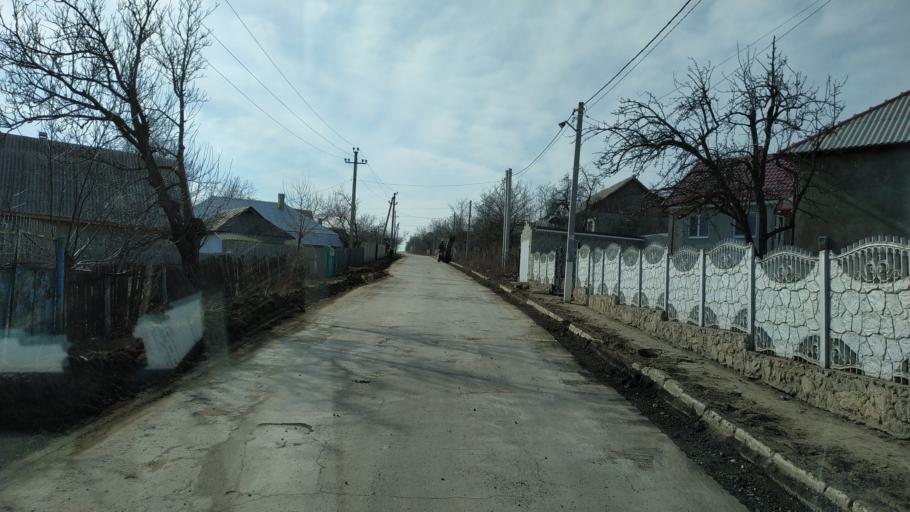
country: MD
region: Nisporeni
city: Nisporeni
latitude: 47.1557
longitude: 28.1322
